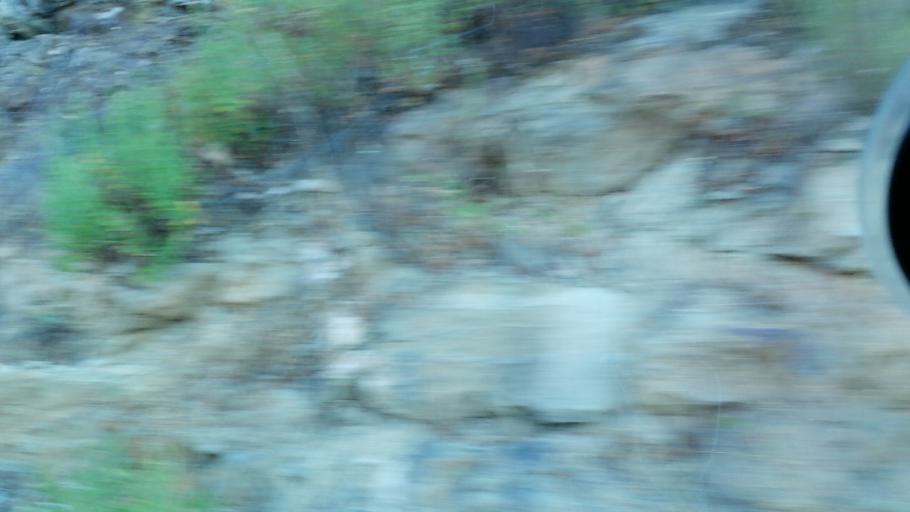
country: PT
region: Viseu
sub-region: Sao Joao da Pesqueira
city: Sao Joao da Pesqueira
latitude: 41.2280
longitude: -7.4245
